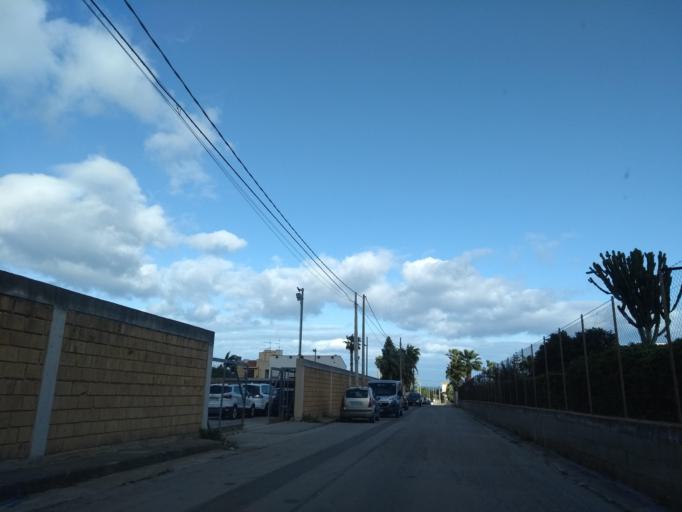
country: IT
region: Sicily
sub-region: Palermo
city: Cinisi
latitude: 38.1686
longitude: 13.1083
